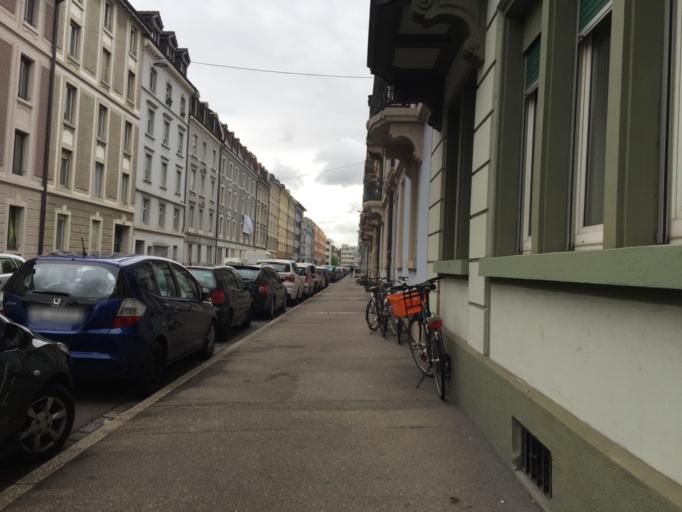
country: CH
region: Basel-Landschaft
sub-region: Bezirk Arlesheim
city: Birsfelden
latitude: 47.5440
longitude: 7.5971
